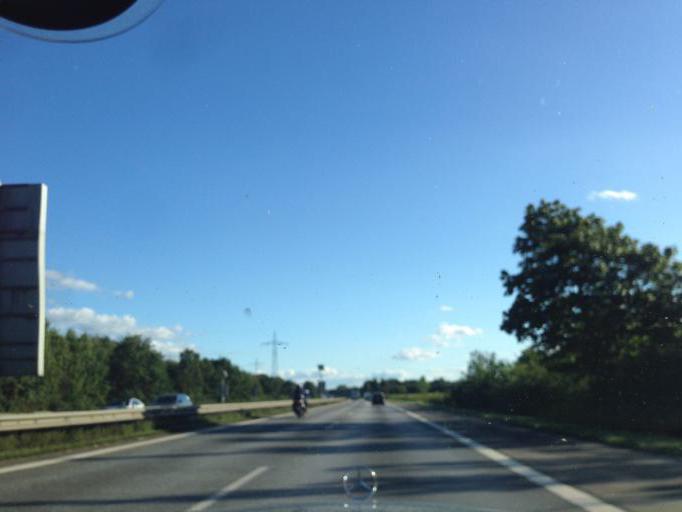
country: DE
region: Schleswig-Holstein
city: Padenstedt
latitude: 54.0593
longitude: 9.9231
